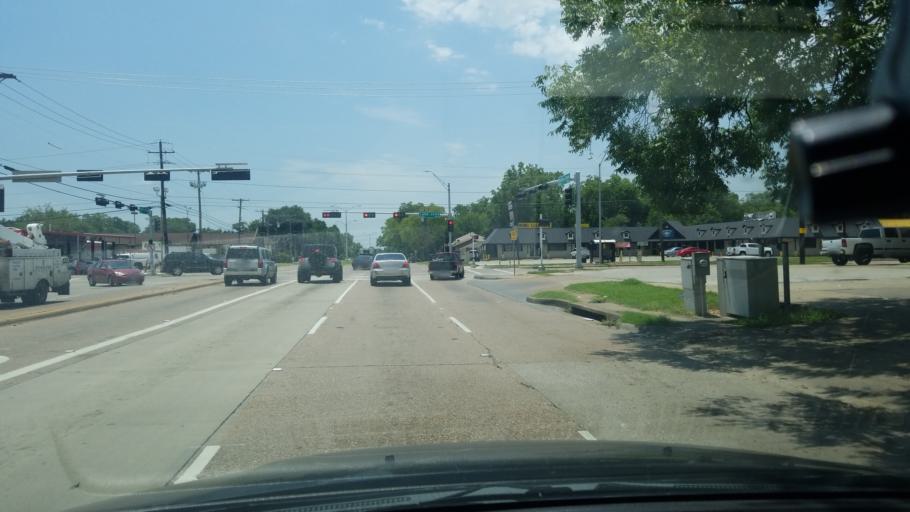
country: US
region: Texas
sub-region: Dallas County
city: Balch Springs
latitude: 32.7347
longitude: -96.6657
